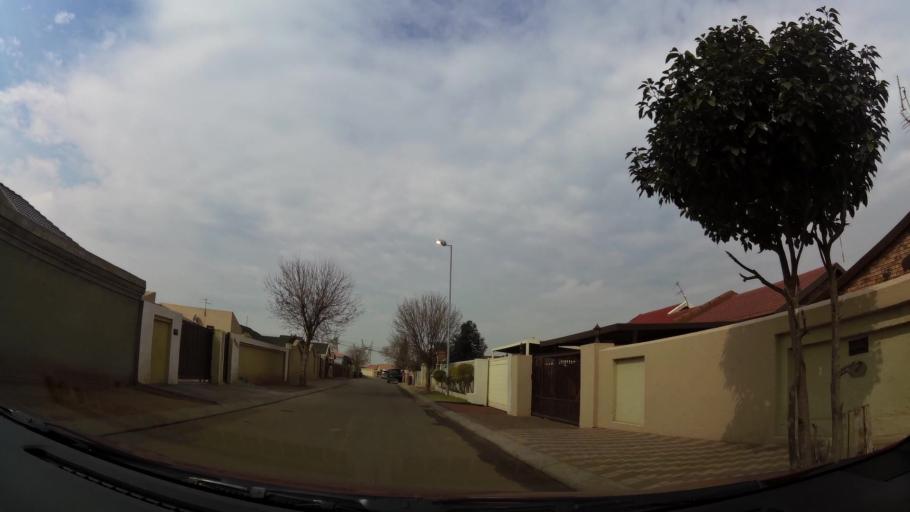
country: ZA
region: Gauteng
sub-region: City of Johannesburg Metropolitan Municipality
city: Soweto
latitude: -26.2635
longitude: 27.8257
